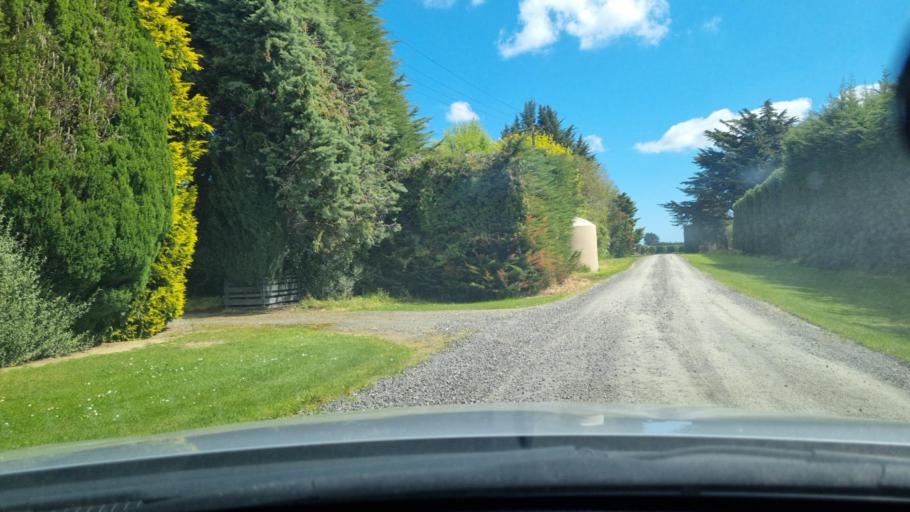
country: NZ
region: Southland
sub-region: Invercargill City
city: Invercargill
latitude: -46.3702
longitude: 168.3272
